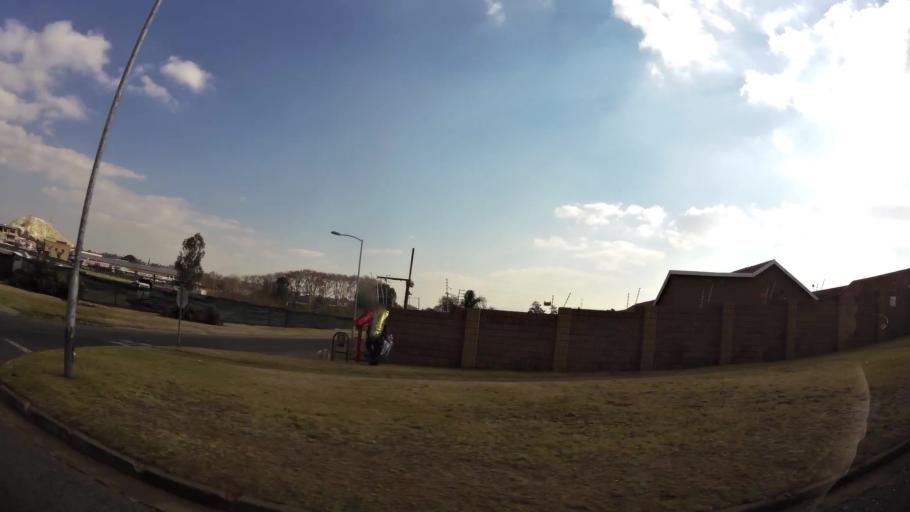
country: ZA
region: Gauteng
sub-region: West Rand District Municipality
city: Krugersdorp
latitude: -26.0955
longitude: 27.7718
